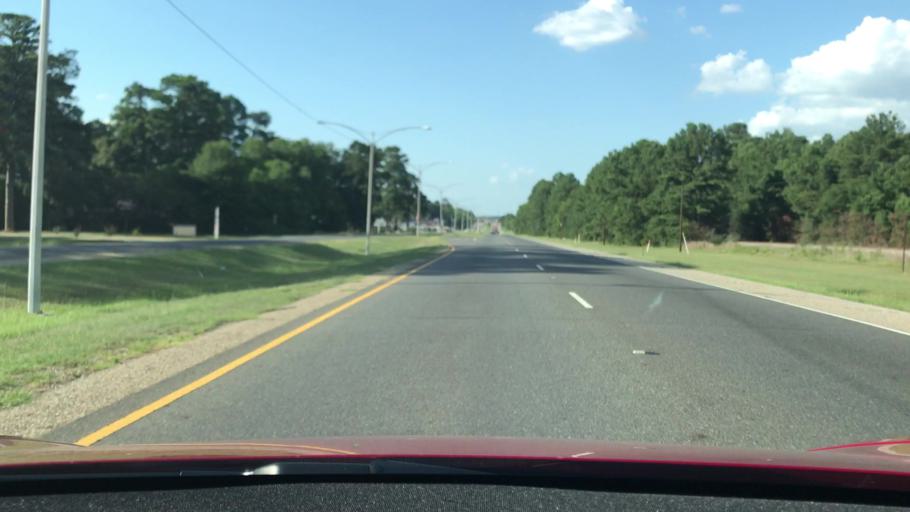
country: US
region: Louisiana
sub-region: Bossier Parish
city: Bossier City
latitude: 32.4209
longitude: -93.7873
